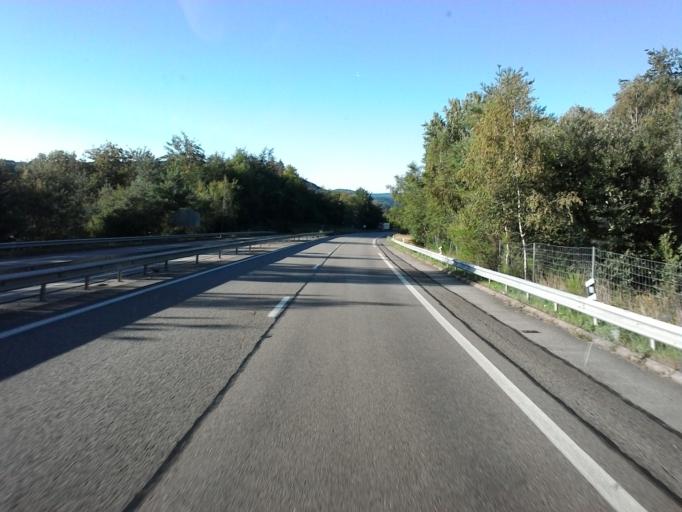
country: FR
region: Lorraine
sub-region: Departement des Vosges
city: Remiremont
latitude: 48.0151
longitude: 6.5645
